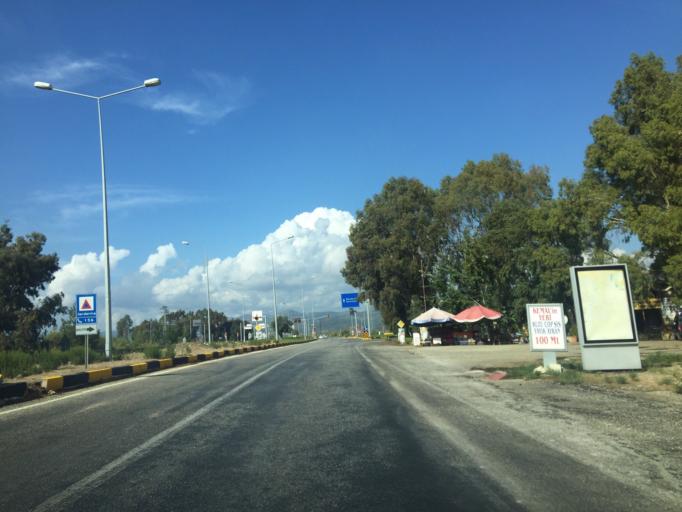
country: TR
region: Izmir
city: Selcuk
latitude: 37.9508
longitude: 27.3004
